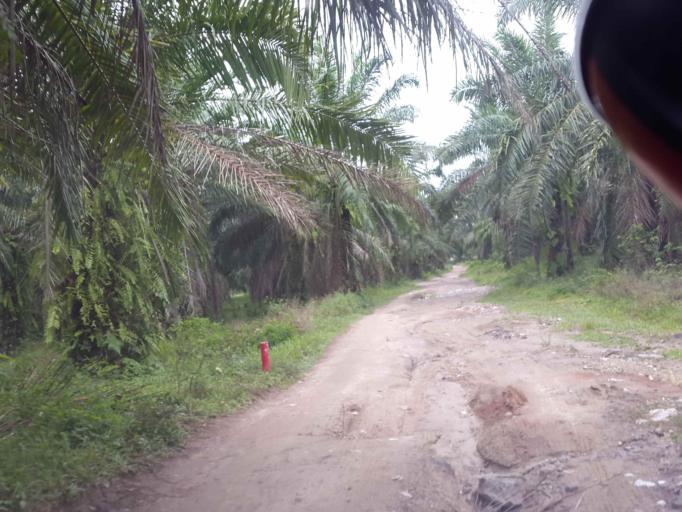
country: ID
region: Lampung
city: Natar
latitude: -5.2732
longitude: 105.2155
